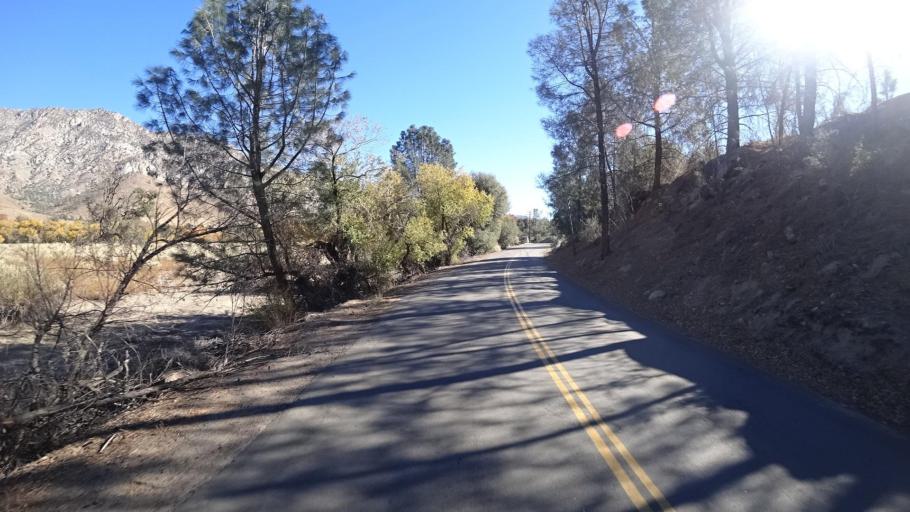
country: US
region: California
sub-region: Kern County
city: Kernville
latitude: 35.7725
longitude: -118.4405
